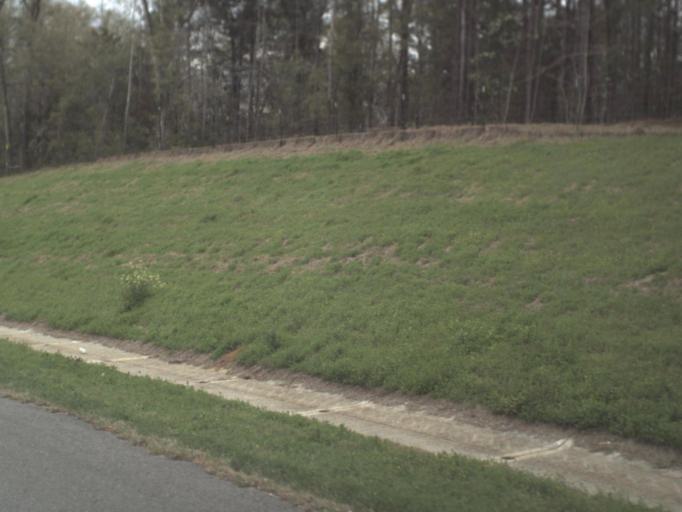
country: US
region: Florida
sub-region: Gadsden County
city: Quincy
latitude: 30.4940
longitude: -84.6119
